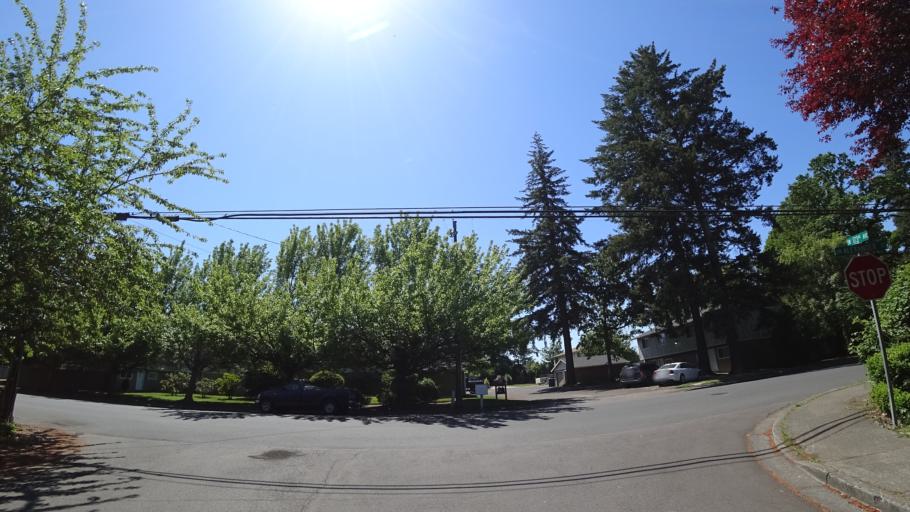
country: US
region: Oregon
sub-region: Washington County
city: Aloha
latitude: 45.4941
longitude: -122.8552
